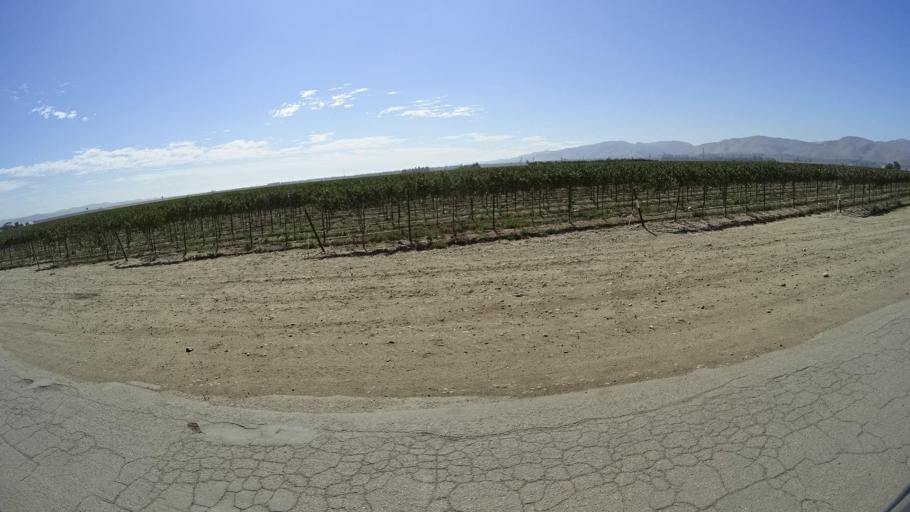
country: US
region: California
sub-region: Monterey County
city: Greenfield
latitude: 36.3117
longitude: -121.2247
